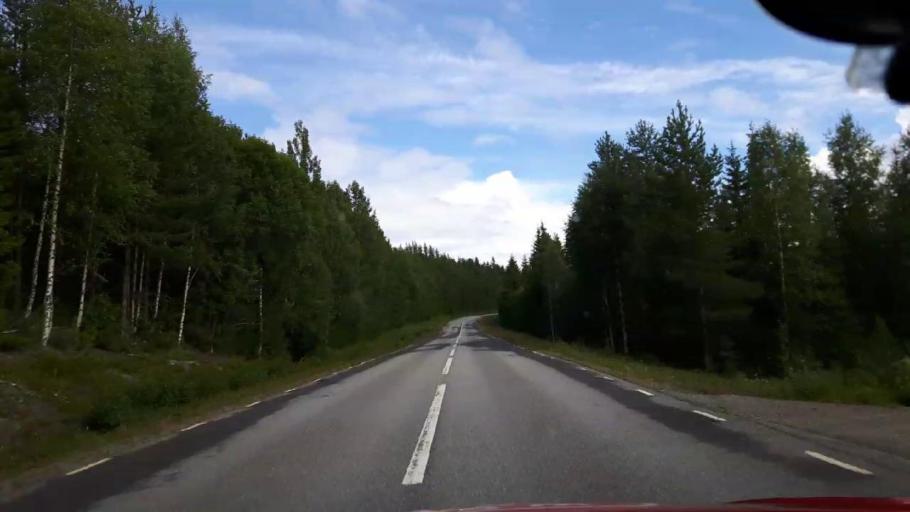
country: SE
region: Jaemtland
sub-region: Stroemsunds Kommun
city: Stroemsund
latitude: 64.3473
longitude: 15.0742
